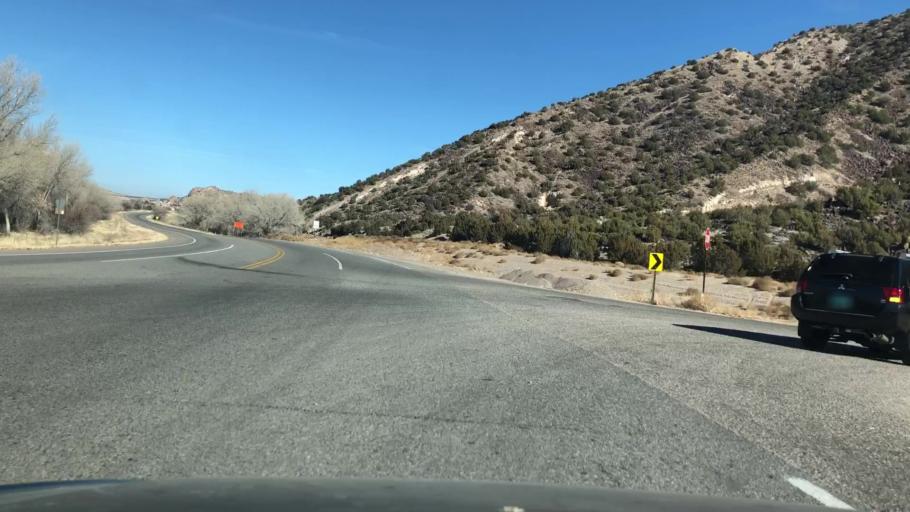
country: US
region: New Mexico
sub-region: Rio Arriba County
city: Ohkay Owingeh
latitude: 36.0963
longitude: -106.1302
